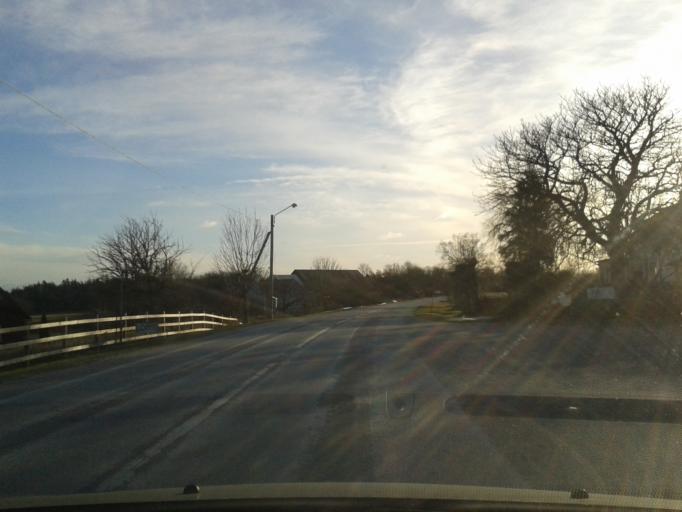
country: SE
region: Gotland
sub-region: Gotland
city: Hemse
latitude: 57.4283
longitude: 18.6314
